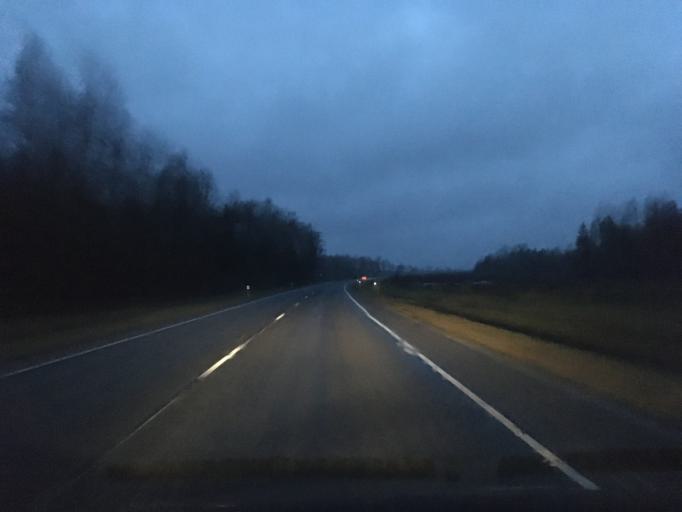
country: EE
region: Harju
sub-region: Nissi vald
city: Turba
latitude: 58.9724
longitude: 24.0621
